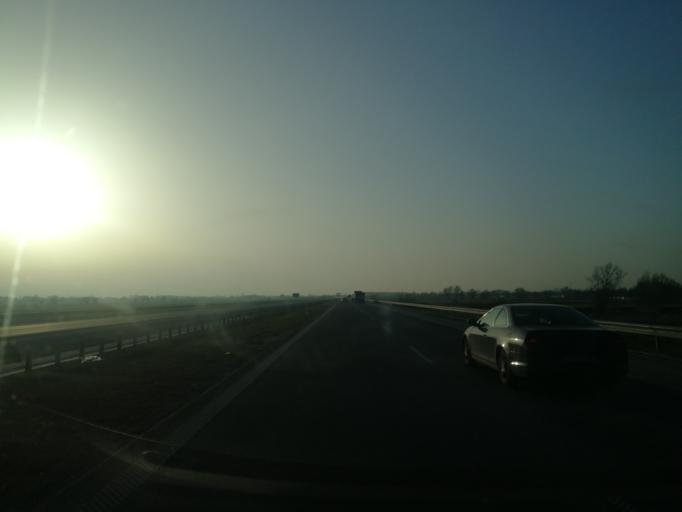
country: PL
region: Warmian-Masurian Voivodeship
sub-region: Powiat elblaski
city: Gronowo Elblaskie
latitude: 54.1643
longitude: 19.2921
